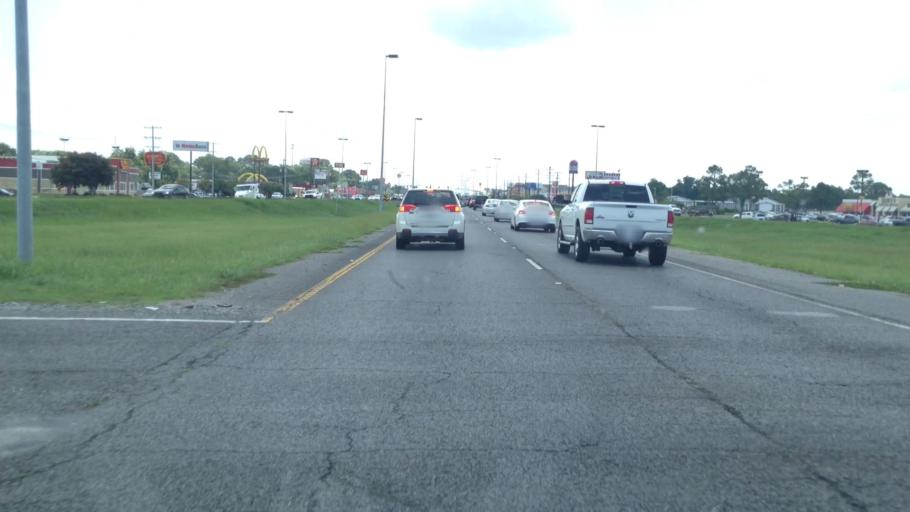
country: US
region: Louisiana
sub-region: Rapides Parish
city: Alexandria
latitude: 31.2989
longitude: -92.4800
